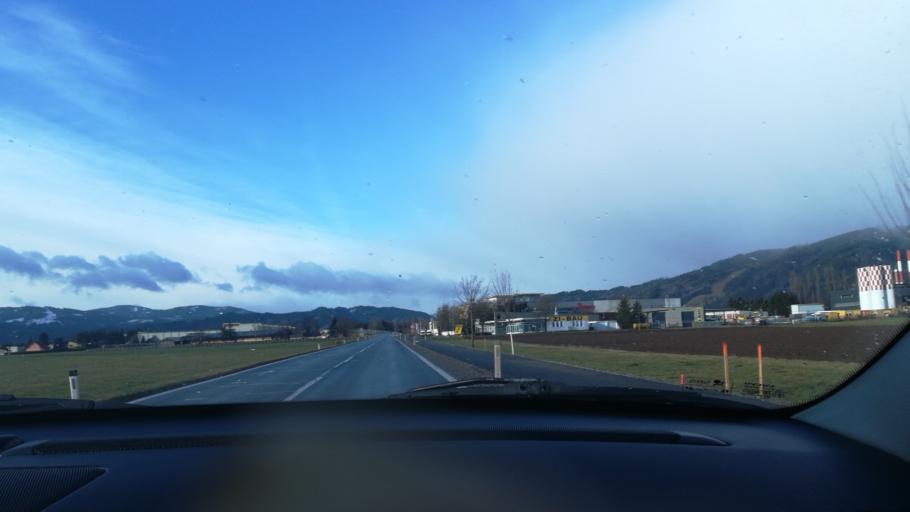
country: AT
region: Styria
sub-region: Politischer Bezirk Murtal
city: Zeltweg
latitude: 47.1950
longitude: 14.7363
